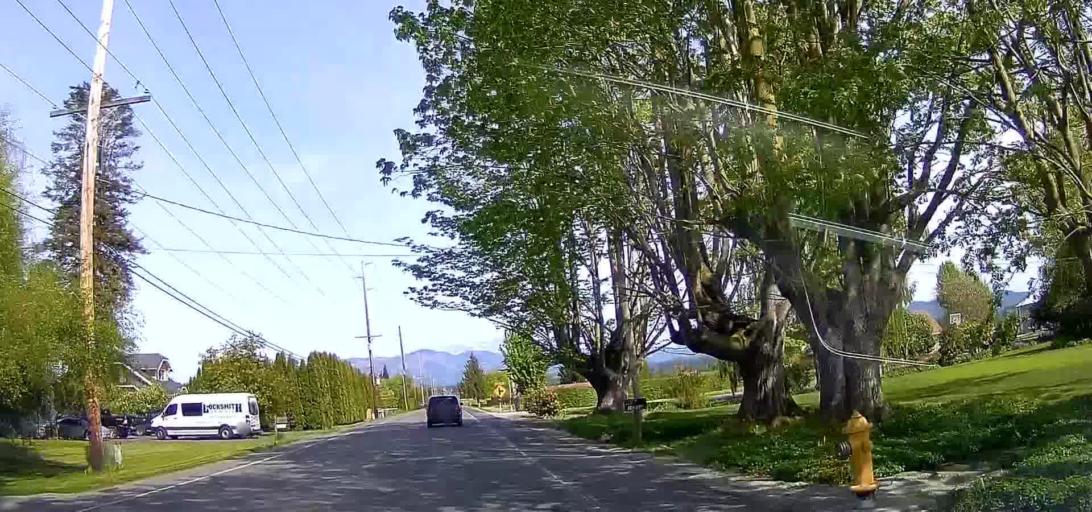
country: US
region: Washington
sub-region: Skagit County
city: Mount Vernon
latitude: 48.4209
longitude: -122.3876
